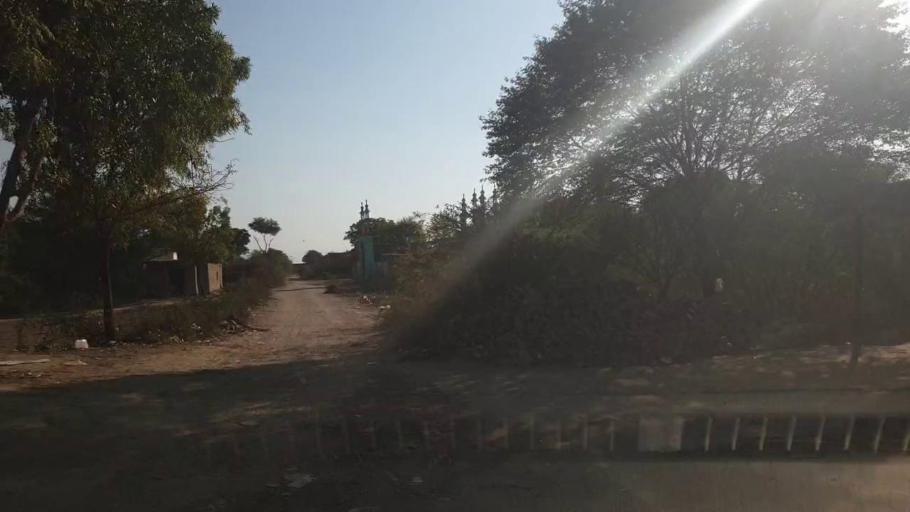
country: PK
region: Sindh
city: Chambar
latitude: 25.2942
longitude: 68.7688
